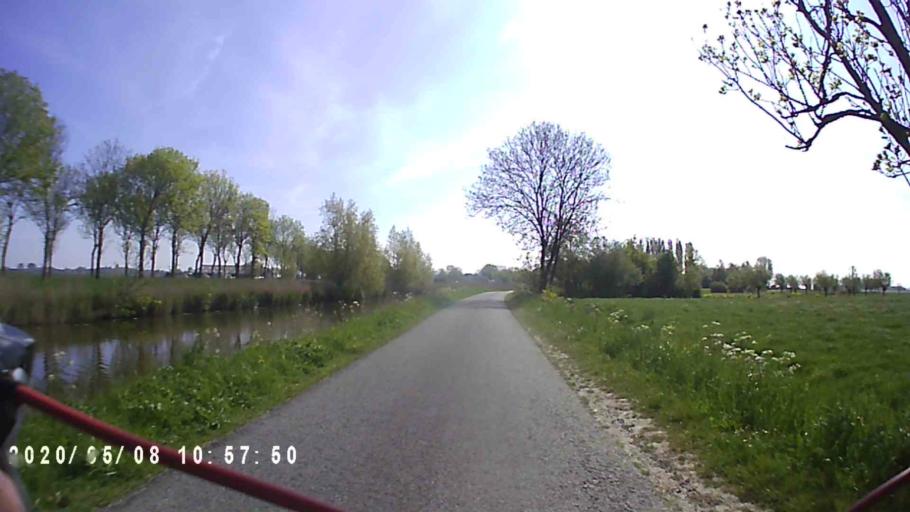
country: NL
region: Groningen
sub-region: Gemeente Bedum
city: Bedum
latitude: 53.3376
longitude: 6.6121
